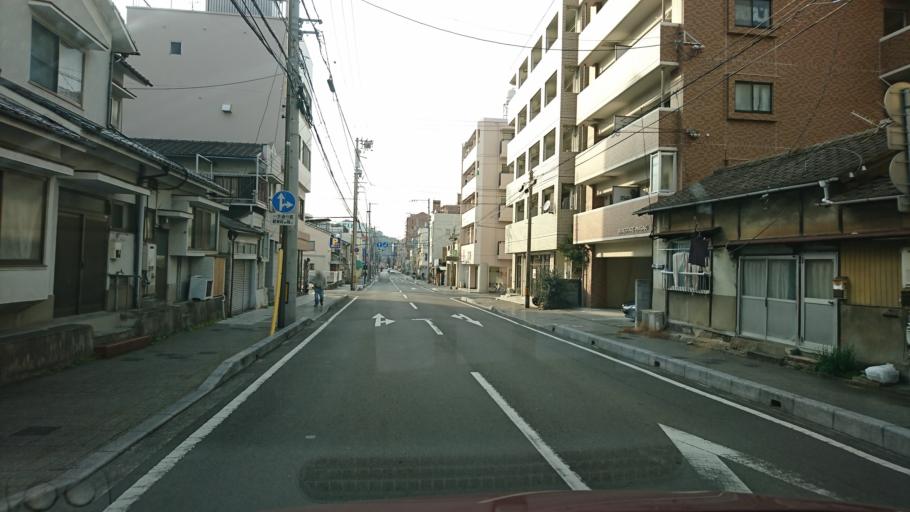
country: JP
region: Ehime
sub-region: Shikoku-chuo Shi
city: Matsuyama
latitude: 33.8455
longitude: 132.7582
